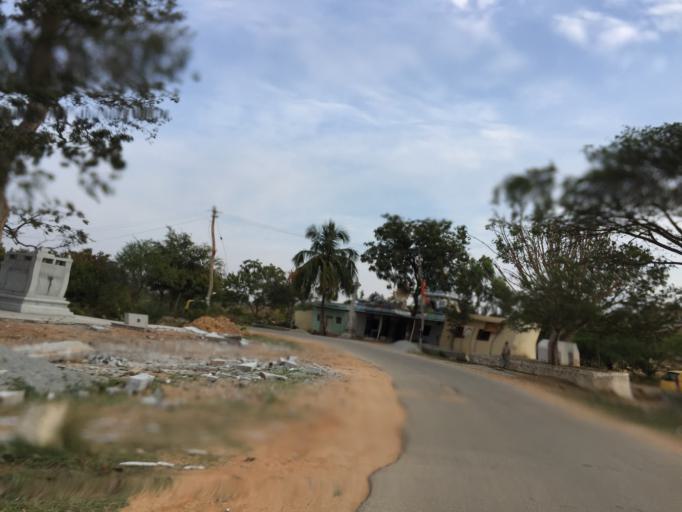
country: IN
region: Karnataka
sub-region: Kolar
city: Kolar
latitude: 13.1398
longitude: 78.1057
